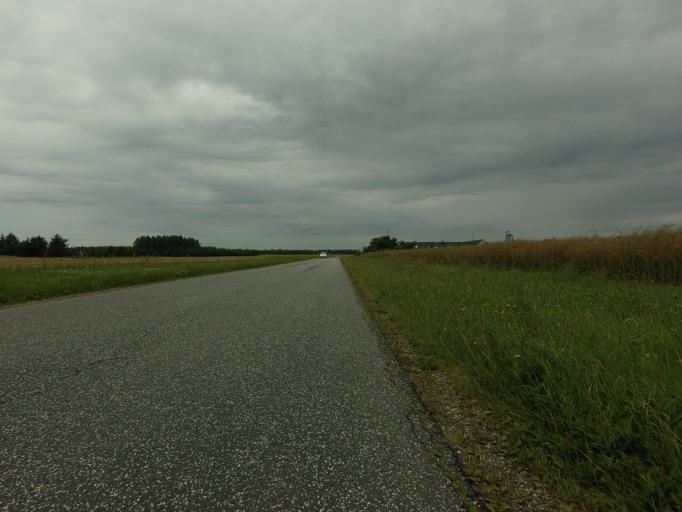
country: DK
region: North Denmark
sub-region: Alborg Kommune
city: Vadum
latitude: 57.1284
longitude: 9.8543
